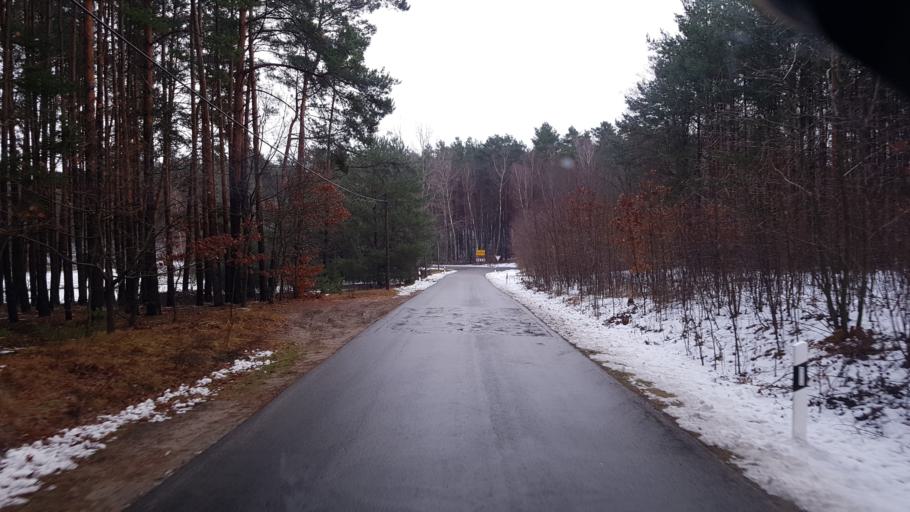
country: DE
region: Brandenburg
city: Lieberose
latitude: 51.9729
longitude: 14.2020
